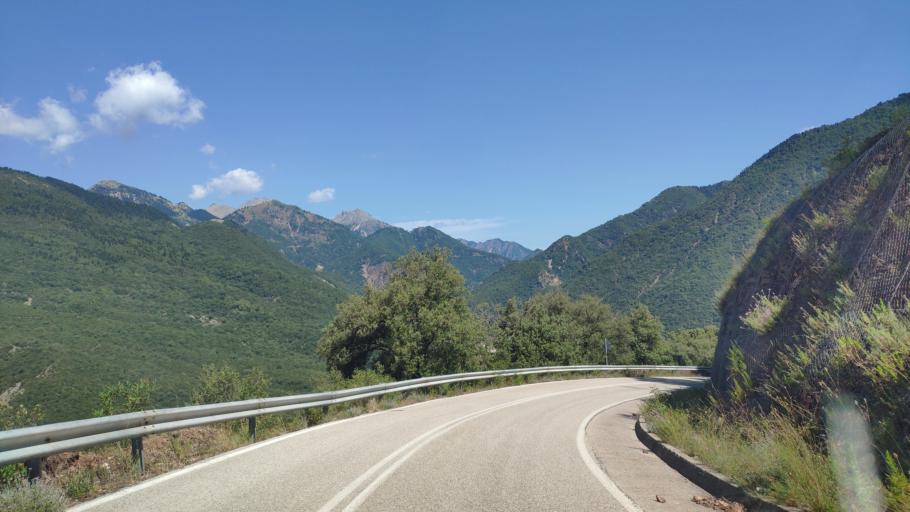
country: GR
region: Central Greece
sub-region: Nomos Evrytanias
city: Kerasochori
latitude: 39.0148
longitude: 21.5969
